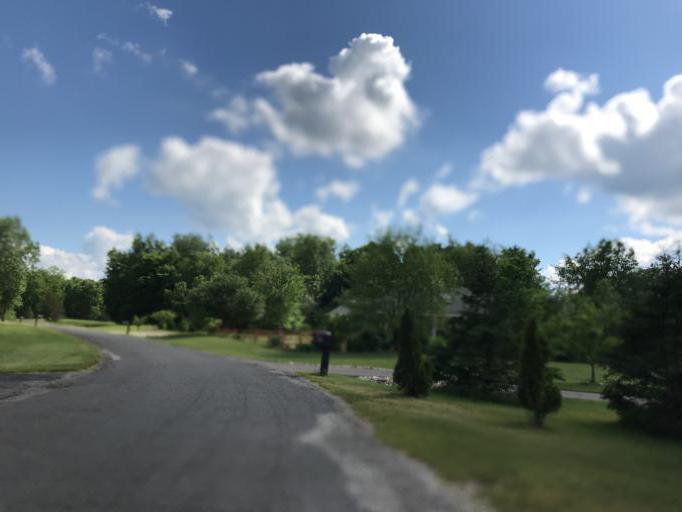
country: US
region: Michigan
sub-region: Oakland County
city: South Lyon
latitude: 42.4276
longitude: -83.6586
